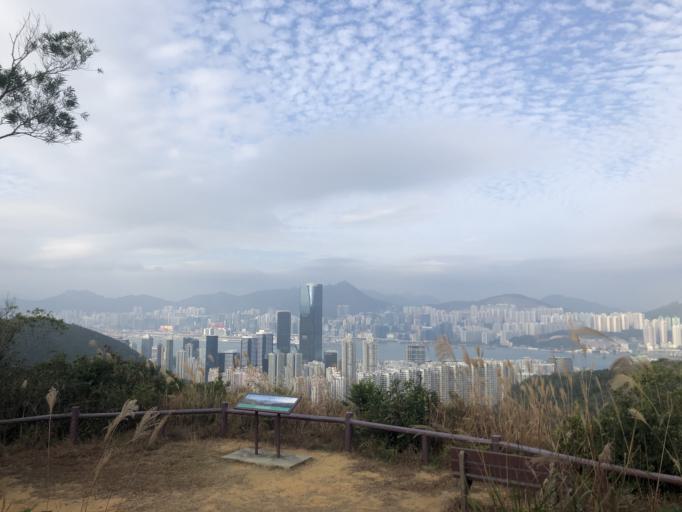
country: HK
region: Wanchai
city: Wan Chai
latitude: 22.2724
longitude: 114.2120
